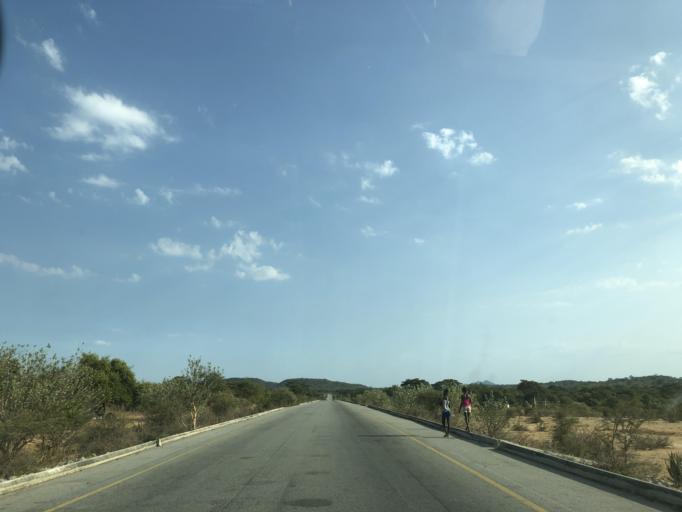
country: AO
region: Benguela
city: Benguela
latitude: -13.2253
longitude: 13.7681
